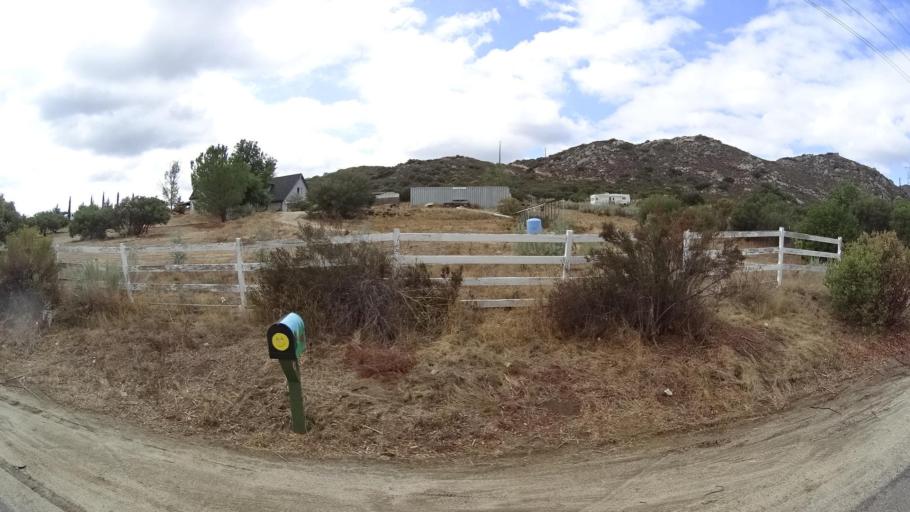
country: US
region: California
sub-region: San Diego County
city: Campo
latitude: 32.6516
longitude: -116.4875
